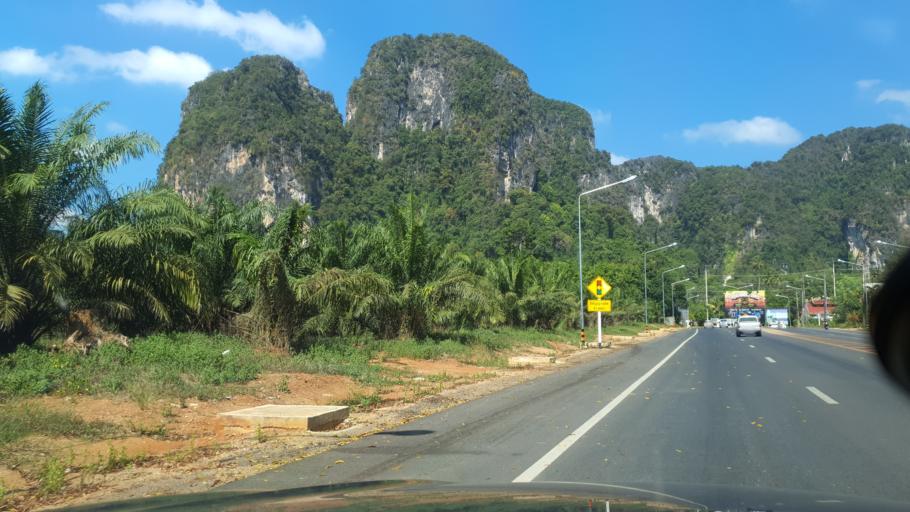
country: TH
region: Krabi
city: Krabi
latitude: 8.0779
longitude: 98.8568
